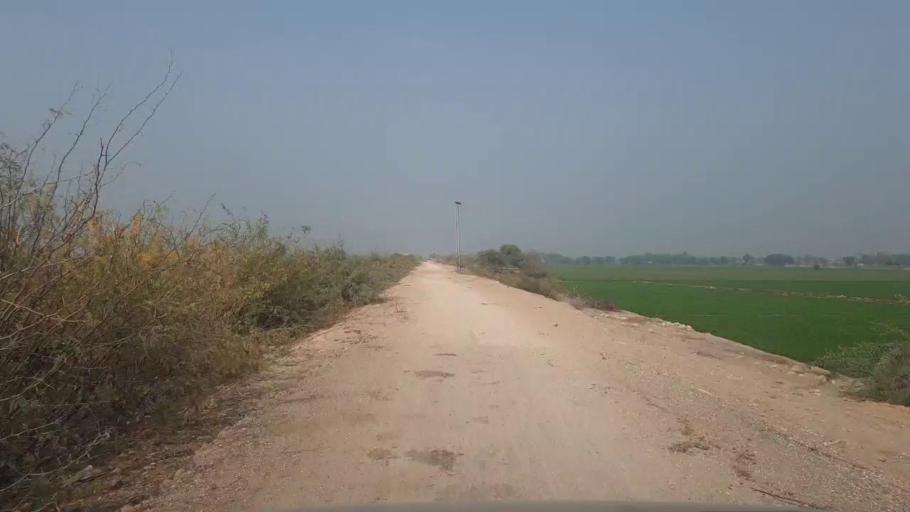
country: PK
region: Sindh
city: Hala
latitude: 25.8140
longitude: 68.4013
